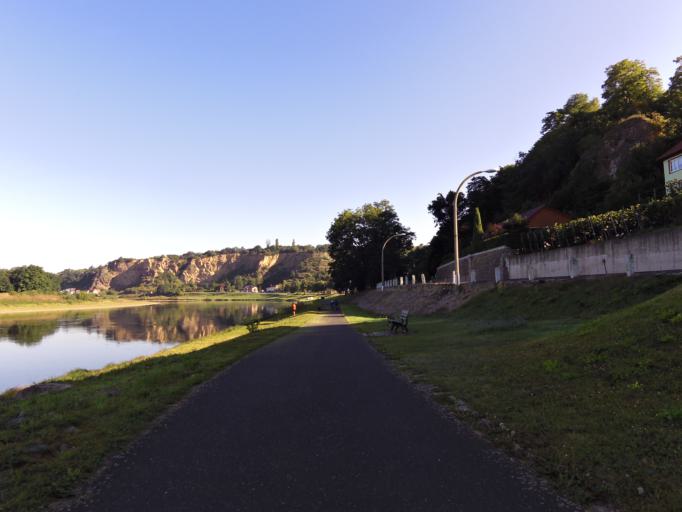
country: DE
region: Saxony
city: Weissig
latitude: 51.2287
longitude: 13.4263
